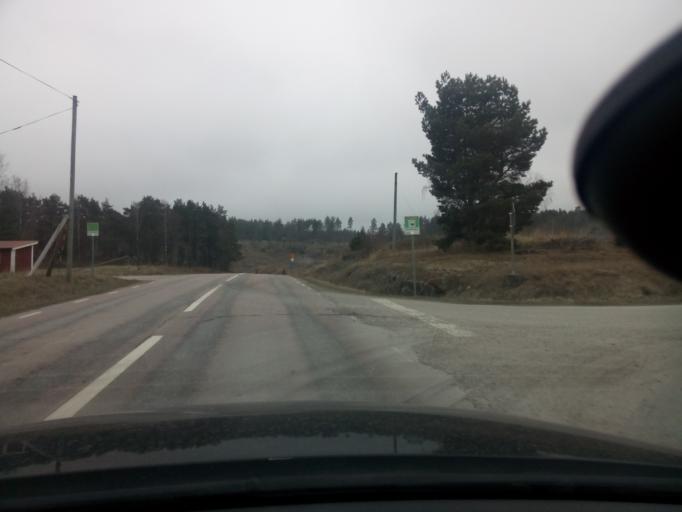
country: SE
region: Soedermanland
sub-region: Gnesta Kommun
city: Gnesta
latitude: 59.0495
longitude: 17.1553
